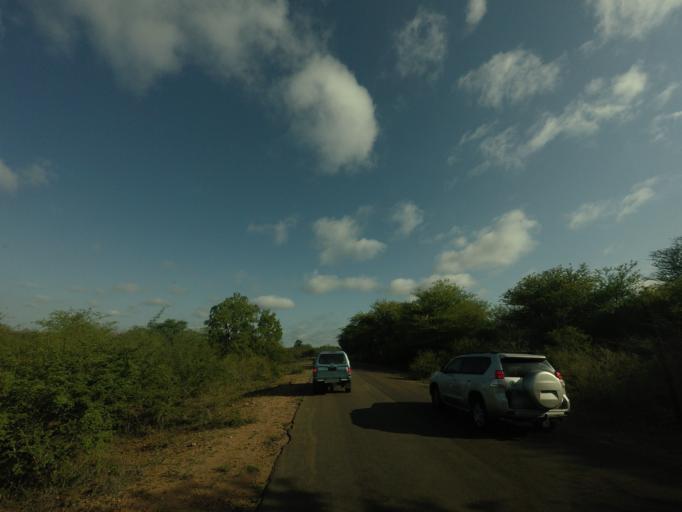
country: ZA
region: Mpumalanga
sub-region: Ehlanzeni District
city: Komatipoort
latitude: -25.2558
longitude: 31.8468
